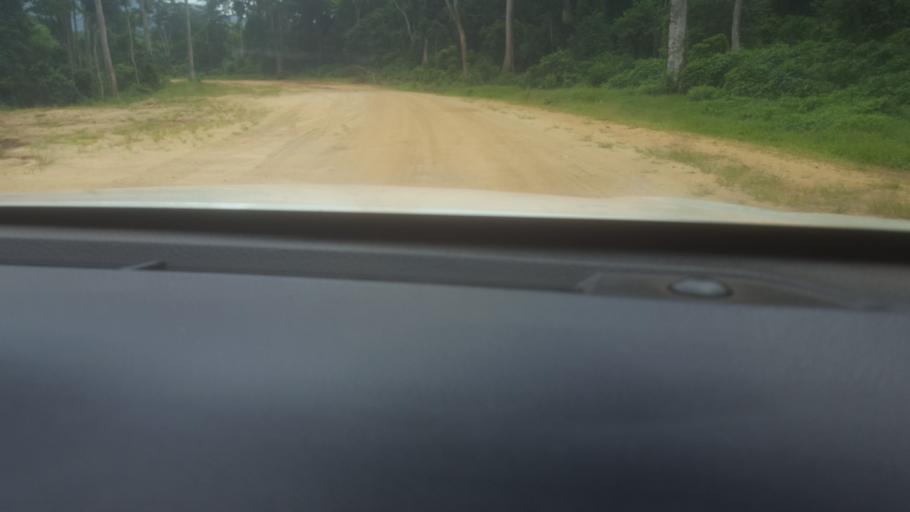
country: ET
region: Southern Nations, Nationalities, and People's Region
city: Tippi
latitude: 7.5101
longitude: 35.0061
